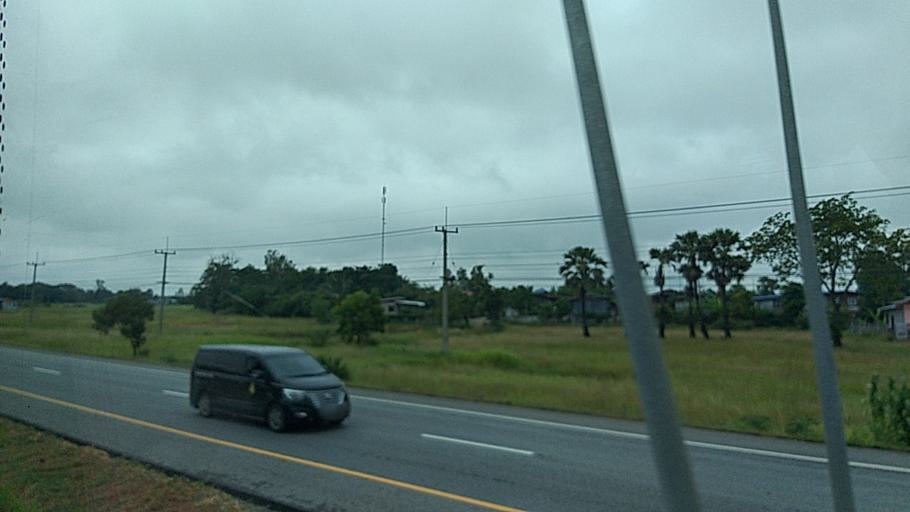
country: TH
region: Nakhon Ratchasima
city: Non Daeng
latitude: 15.4161
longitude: 102.4811
